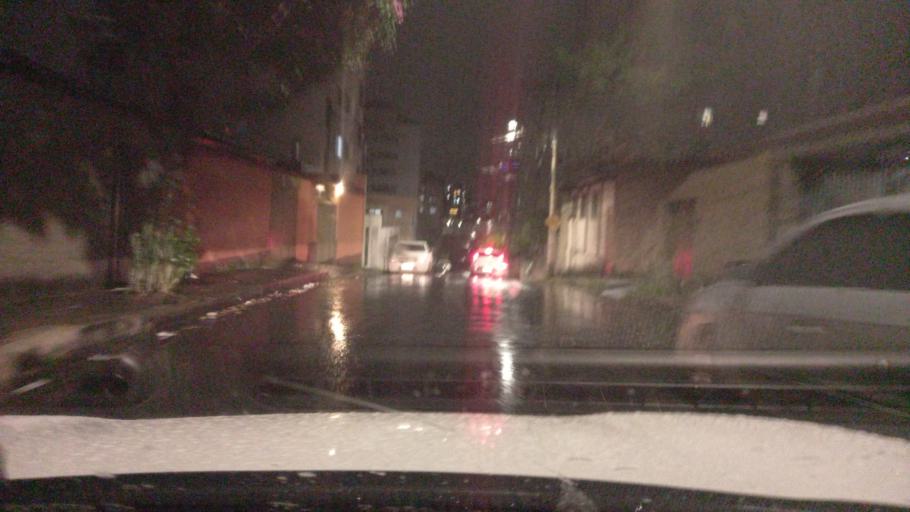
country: BR
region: Minas Gerais
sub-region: Belo Horizonte
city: Belo Horizonte
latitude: -19.8974
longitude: -43.9238
